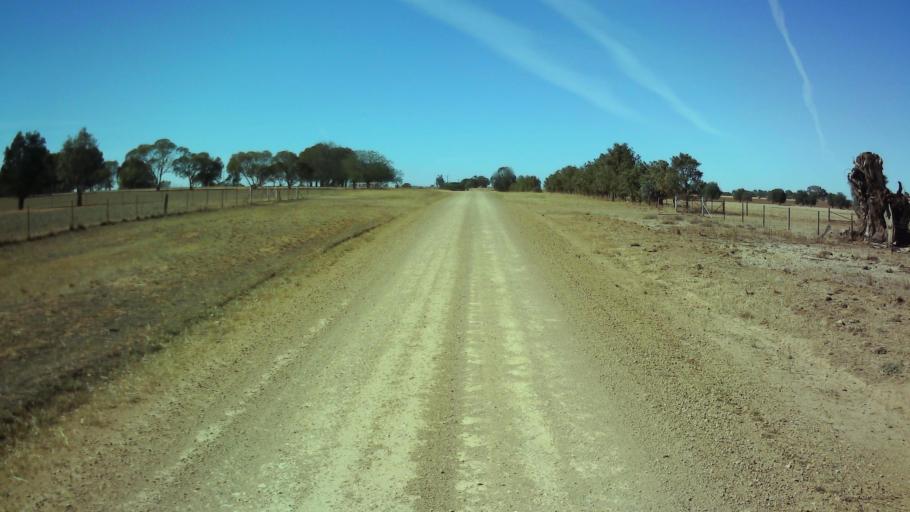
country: AU
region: New South Wales
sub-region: Weddin
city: Grenfell
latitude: -34.0544
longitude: 148.1721
